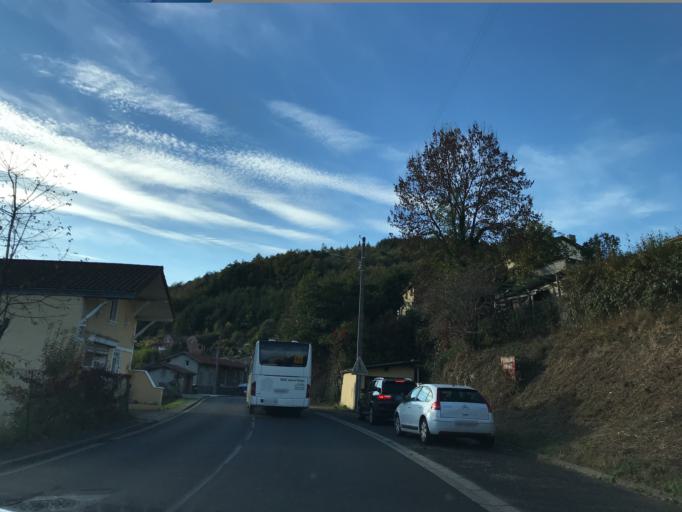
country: FR
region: Auvergne
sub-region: Departement du Puy-de-Dome
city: Celles-sur-Durolle
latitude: 45.8710
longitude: 3.6218
